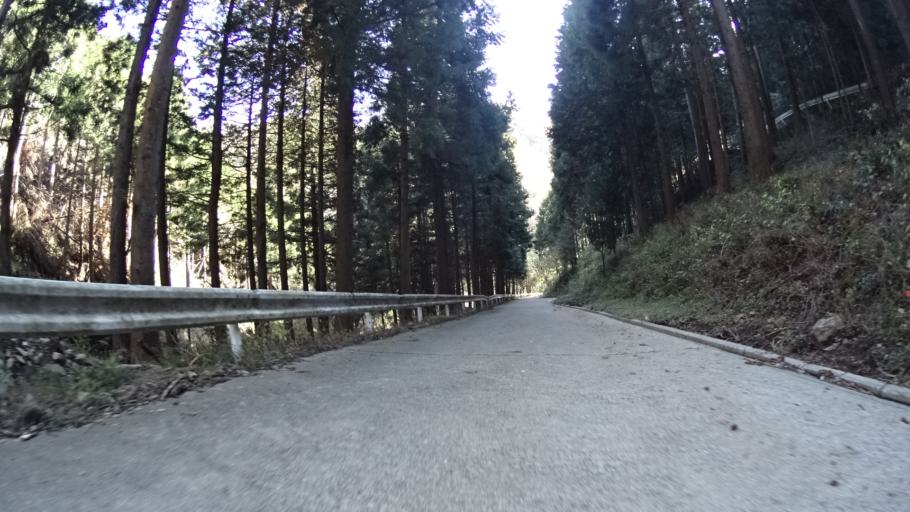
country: JP
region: Kanagawa
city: Atsugi
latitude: 35.5144
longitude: 139.2704
